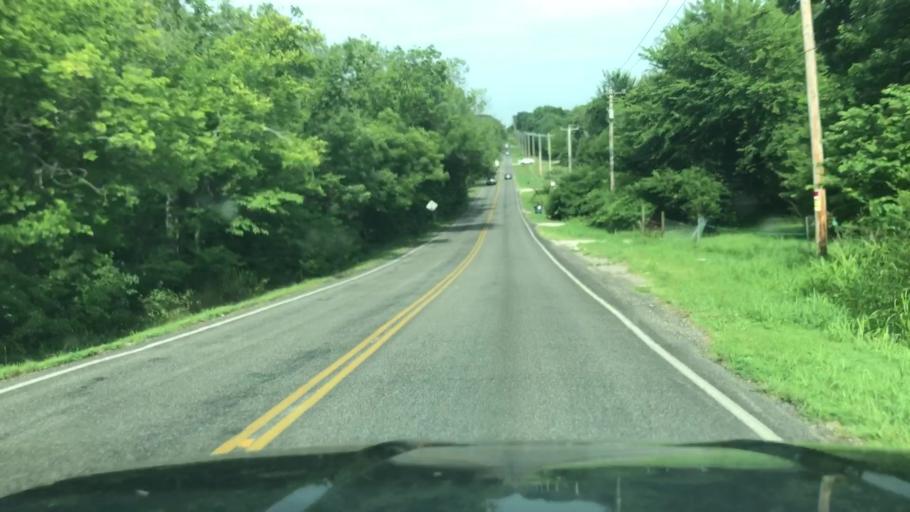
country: US
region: Oklahoma
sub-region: Tulsa County
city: Oakhurst
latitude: 36.0901
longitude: -96.1115
